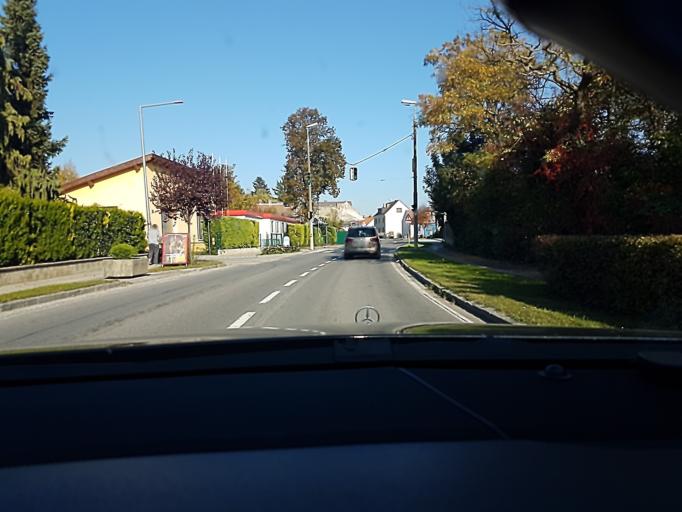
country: AT
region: Lower Austria
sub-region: Politischer Bezirk Wien-Umgebung
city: Lanzendorf
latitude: 48.1089
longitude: 16.4415
